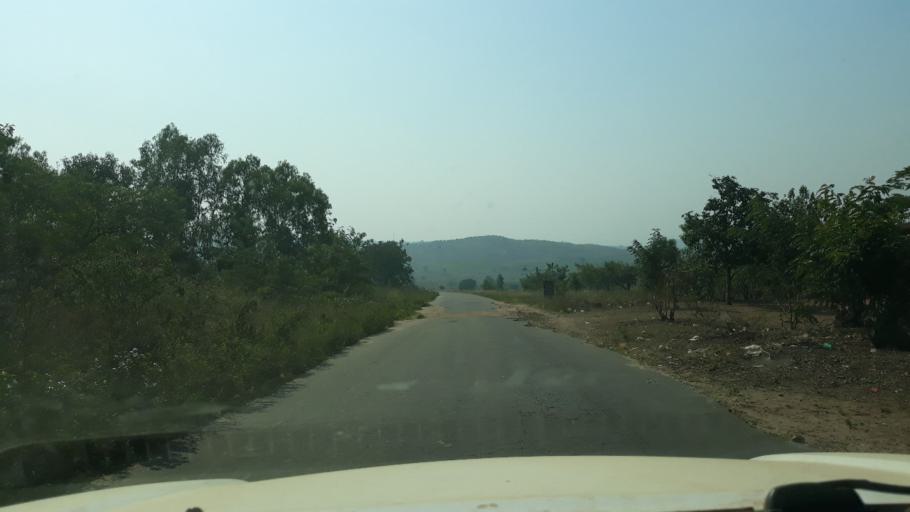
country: BI
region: Cibitoke
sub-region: Commune of Buganda
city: Buganda
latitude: -3.0210
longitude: 29.1075
